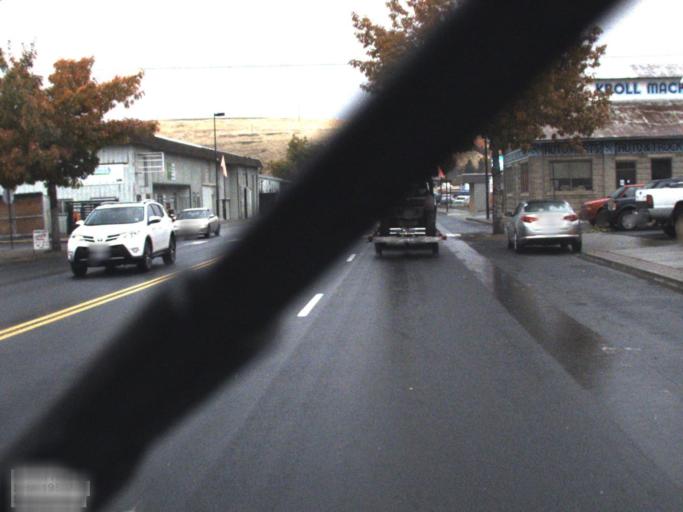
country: US
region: Washington
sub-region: Whitman County
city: Colfax
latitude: 46.8854
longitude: -117.3645
